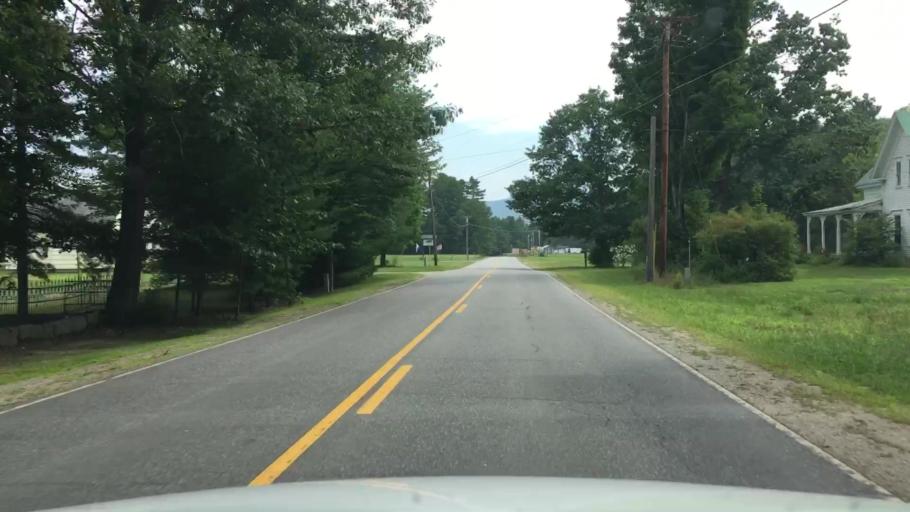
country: US
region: Maine
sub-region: Oxford County
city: Rumford
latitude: 44.6215
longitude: -70.7452
